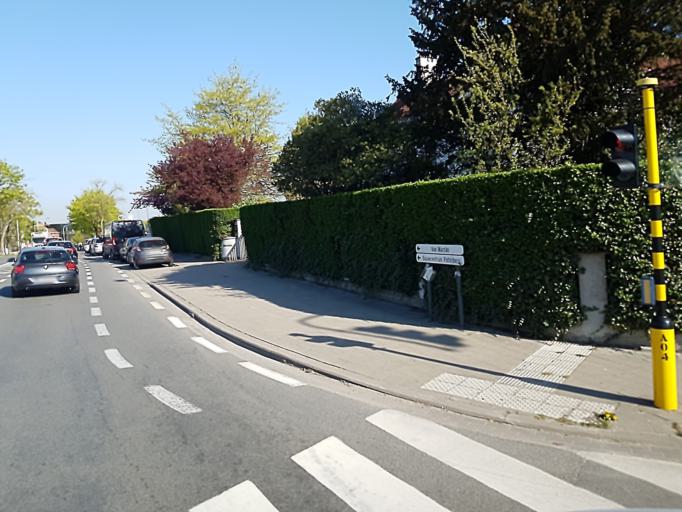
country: BE
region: Flanders
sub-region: Provincie West-Vlaanderen
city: Kortrijk
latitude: 50.8122
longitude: 3.2503
